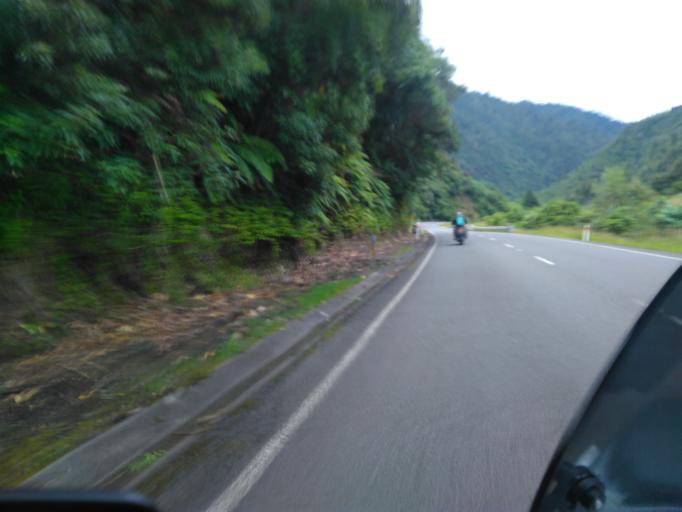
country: NZ
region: Bay of Plenty
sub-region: Opotiki District
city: Opotiki
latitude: -38.2891
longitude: 177.3779
